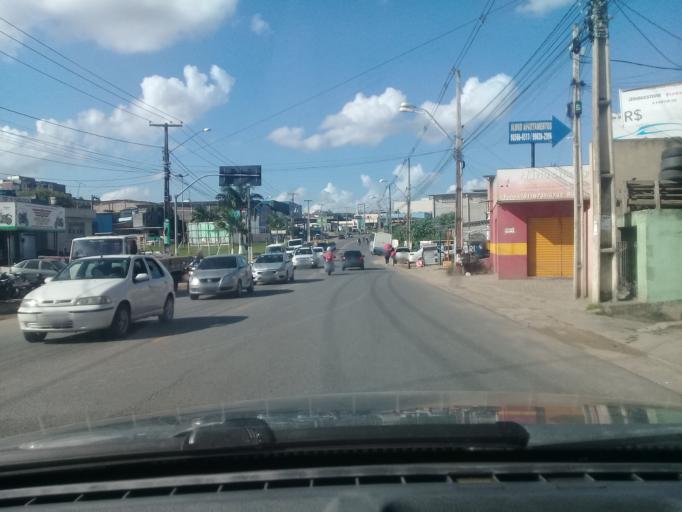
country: BR
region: Pernambuco
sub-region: Vitoria De Santo Antao
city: Vitoria de Santo Antao
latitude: -8.1163
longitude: -35.2965
